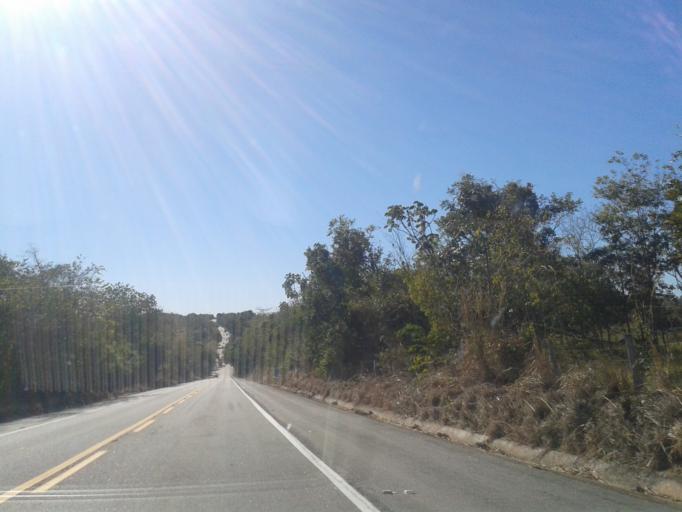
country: BR
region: Goias
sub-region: Itapuranga
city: Itapuranga
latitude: -15.6400
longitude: -50.2262
